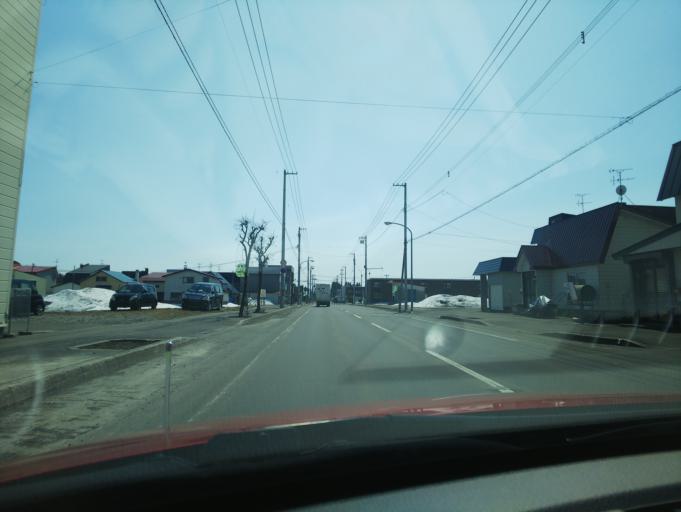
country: JP
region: Hokkaido
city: Nayoro
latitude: 44.3431
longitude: 142.4643
